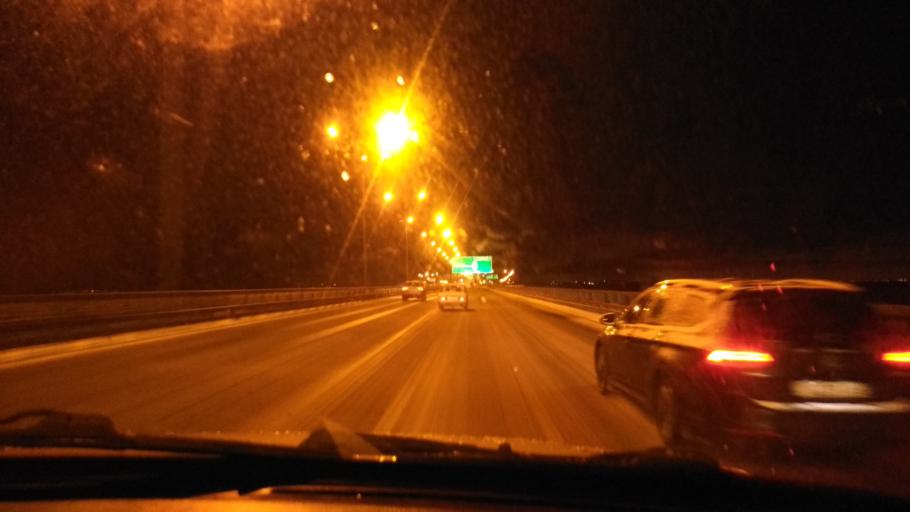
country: RU
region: St.-Petersburg
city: Kronshtadt
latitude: 60.0228
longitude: 29.8066
